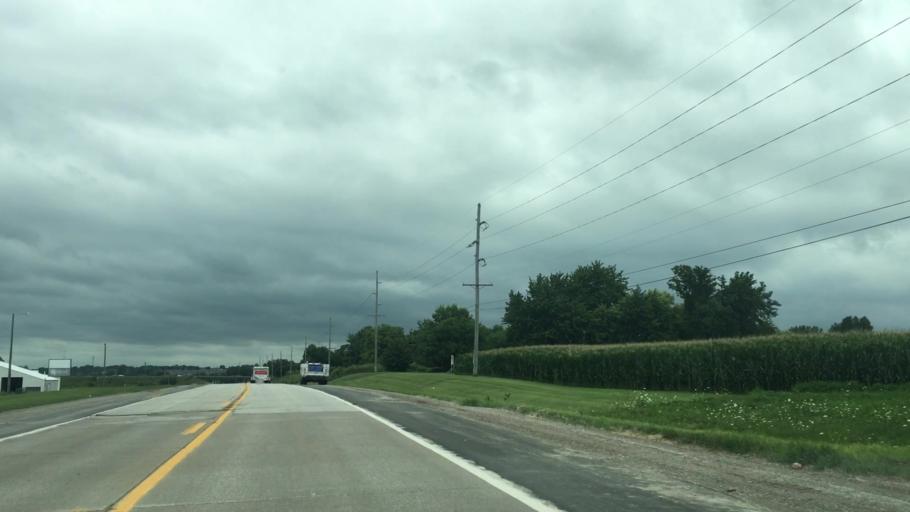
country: US
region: Iowa
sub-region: Johnson County
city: Tiffin
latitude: 41.7026
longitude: -91.6330
